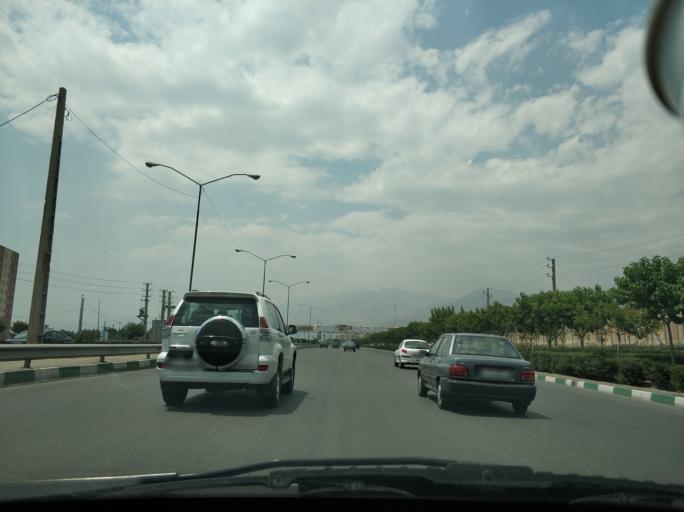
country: IR
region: Tehran
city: Tajrish
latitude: 35.7600
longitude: 51.5723
